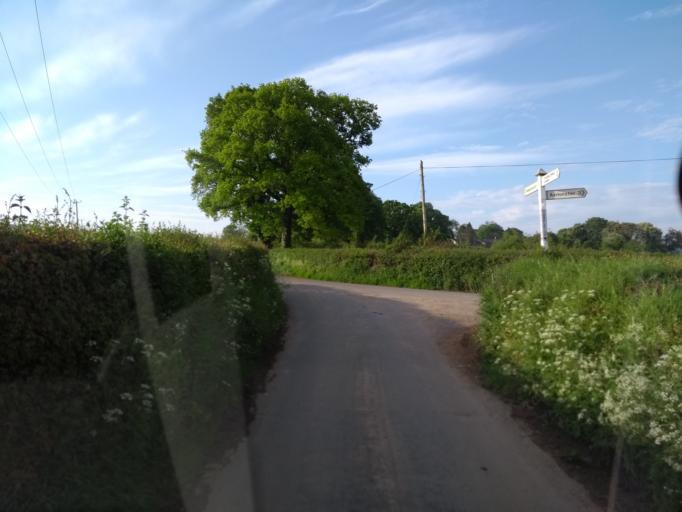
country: GB
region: England
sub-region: Devon
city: Axminster
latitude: 50.8095
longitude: -2.9519
